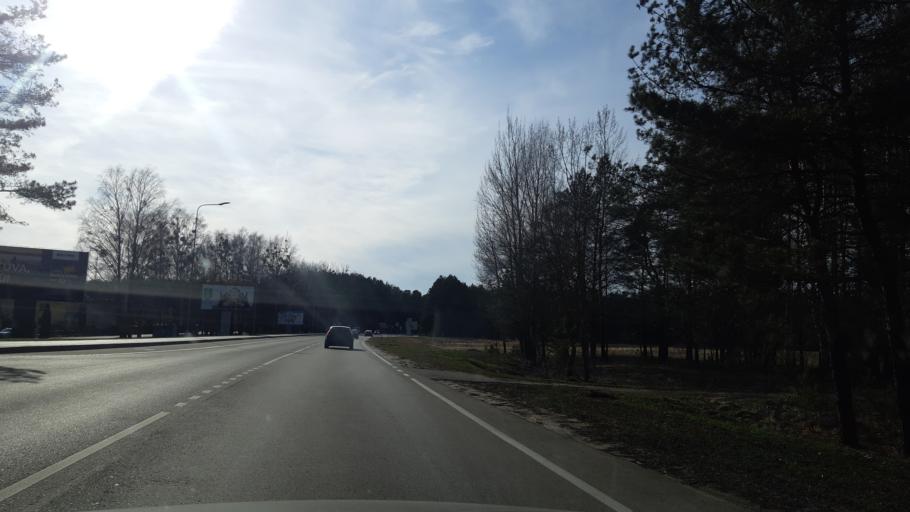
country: LT
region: Alytaus apskritis
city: Druskininkai
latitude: 54.0050
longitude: 24.0179
